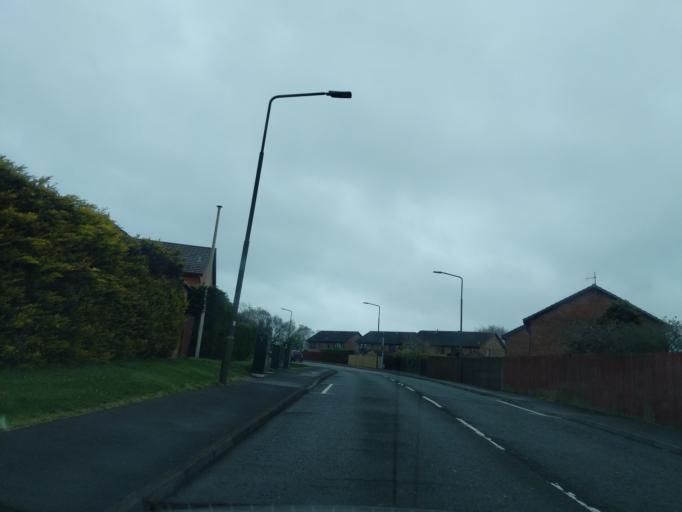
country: GB
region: Scotland
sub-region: East Lothian
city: Musselburgh
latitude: 55.9373
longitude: -3.0732
